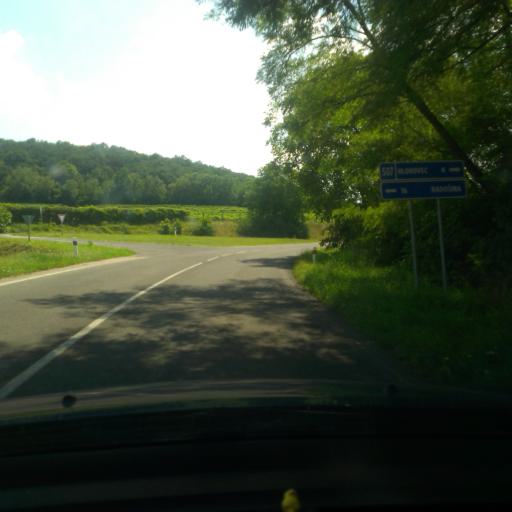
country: SK
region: Trnavsky
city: Hlohovec
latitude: 48.4617
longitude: 17.8157
